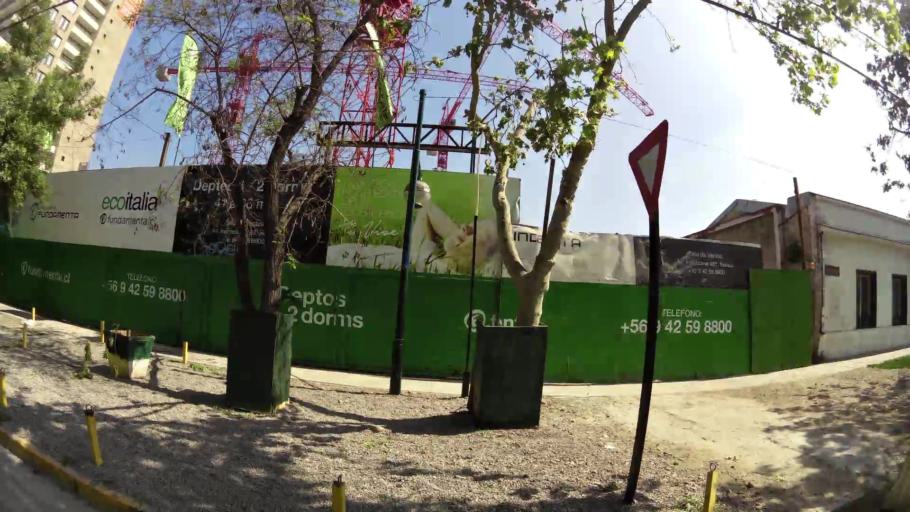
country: CL
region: Santiago Metropolitan
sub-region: Provincia de Santiago
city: Santiago
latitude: -33.4509
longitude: -70.6248
